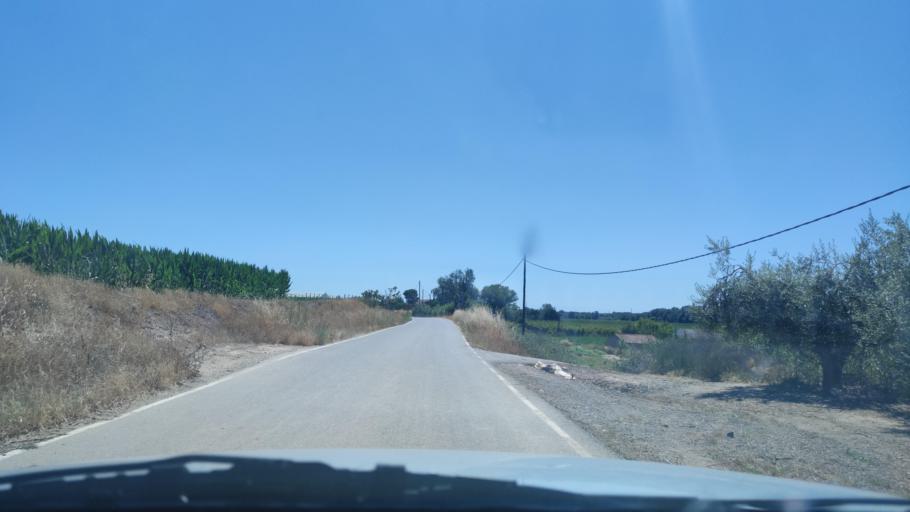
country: ES
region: Catalonia
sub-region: Provincia de Lleida
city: Alcoletge
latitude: 41.6462
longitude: 0.6645
